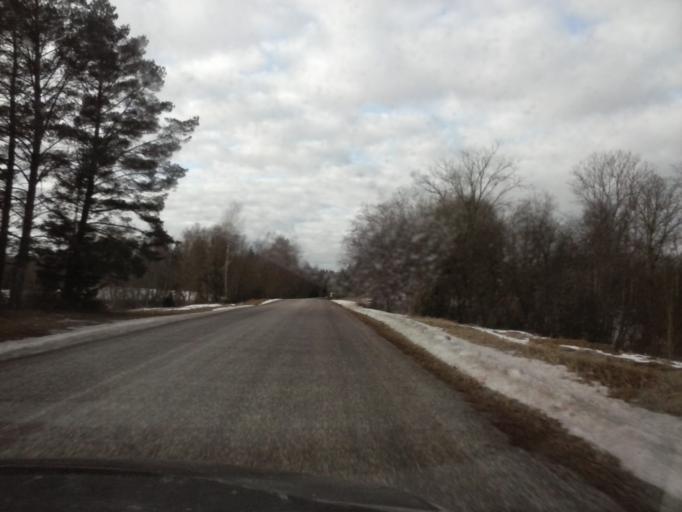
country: EE
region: Tartu
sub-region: Elva linn
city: Elva
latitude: 58.0010
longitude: 26.2736
